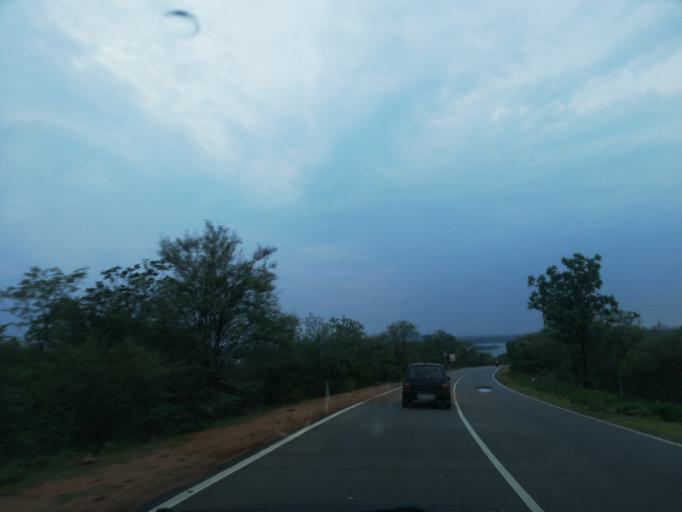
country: IN
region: Andhra Pradesh
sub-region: Guntur
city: Macherla
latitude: 16.6324
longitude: 79.2878
